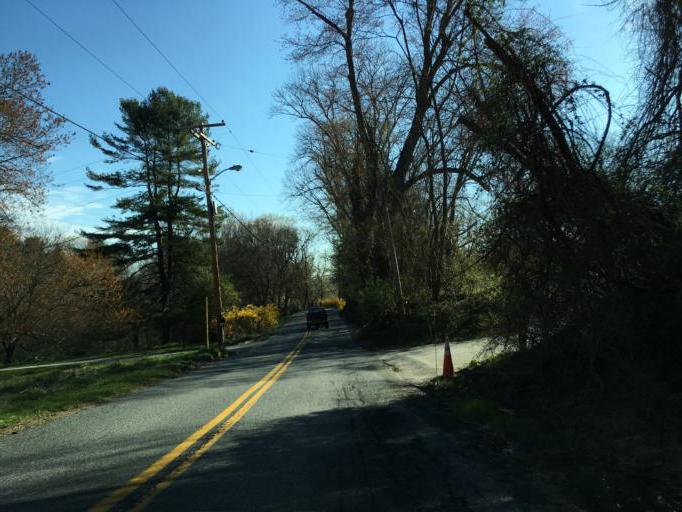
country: US
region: Maryland
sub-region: Baltimore County
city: Hunt Valley
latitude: 39.5206
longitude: -76.6301
